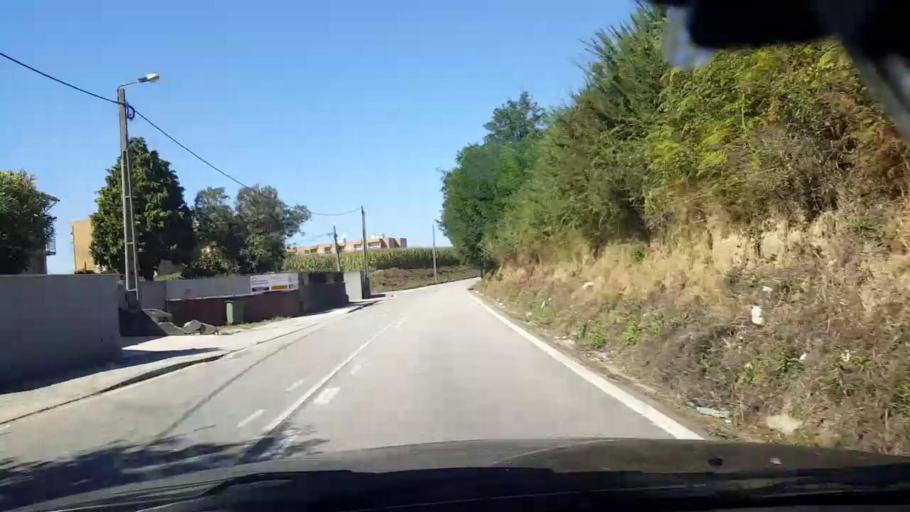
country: PT
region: Porto
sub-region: Vila do Conde
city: Arvore
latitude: 41.3412
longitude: -8.7301
